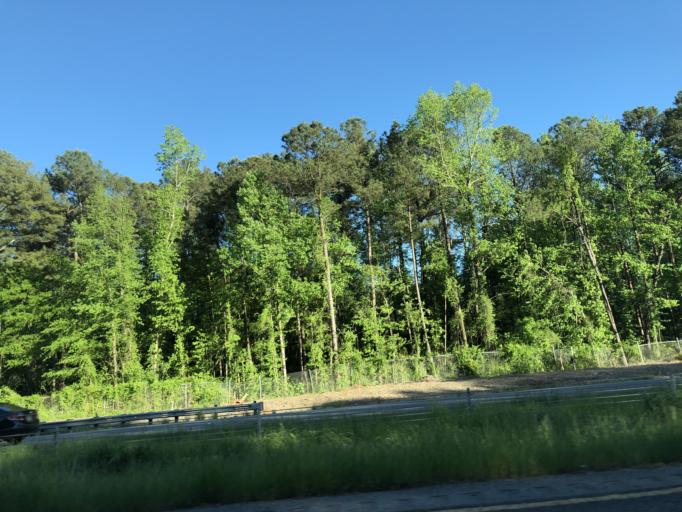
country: US
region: Georgia
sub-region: Clarke County
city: Country Club Estates
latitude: 33.9673
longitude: -83.4234
